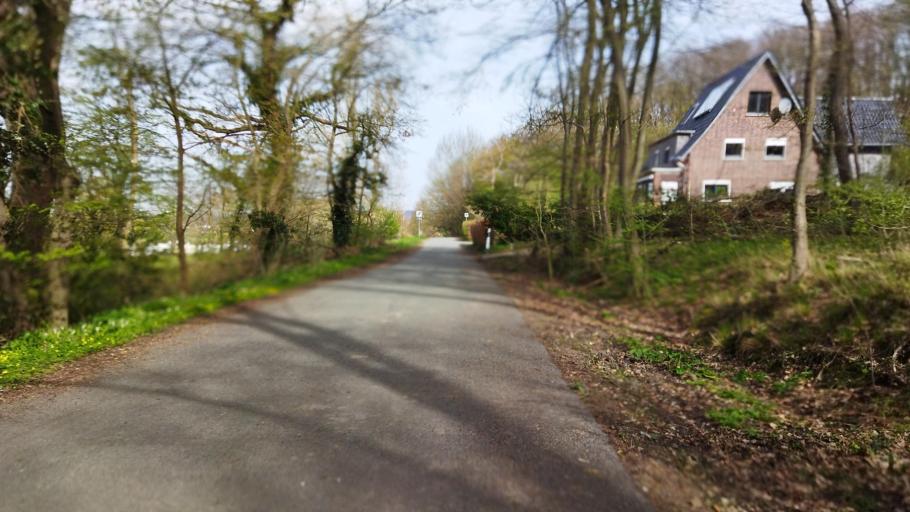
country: DE
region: North Rhine-Westphalia
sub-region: Regierungsbezirk Detmold
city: Vlotho
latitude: 52.2019
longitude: 8.8599
